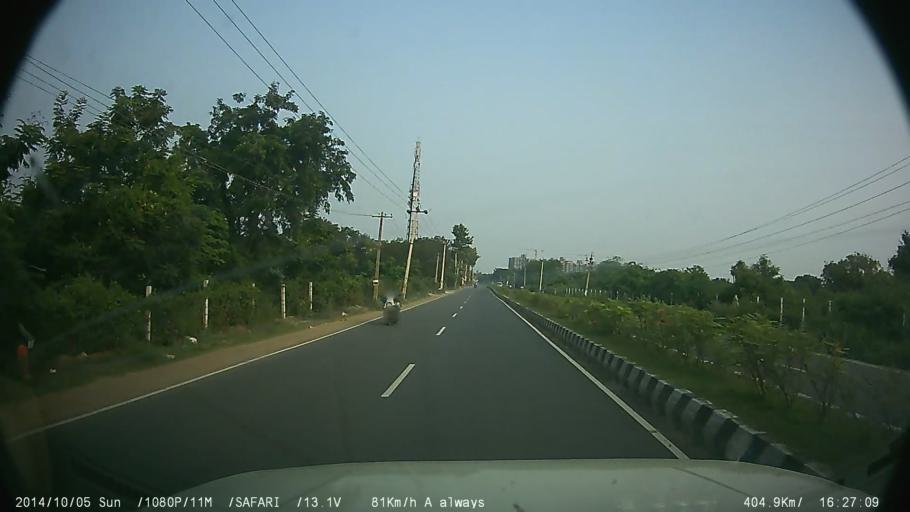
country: IN
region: Tamil Nadu
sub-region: Kancheepuram
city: Vengavasal
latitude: 12.8023
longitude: 80.1941
